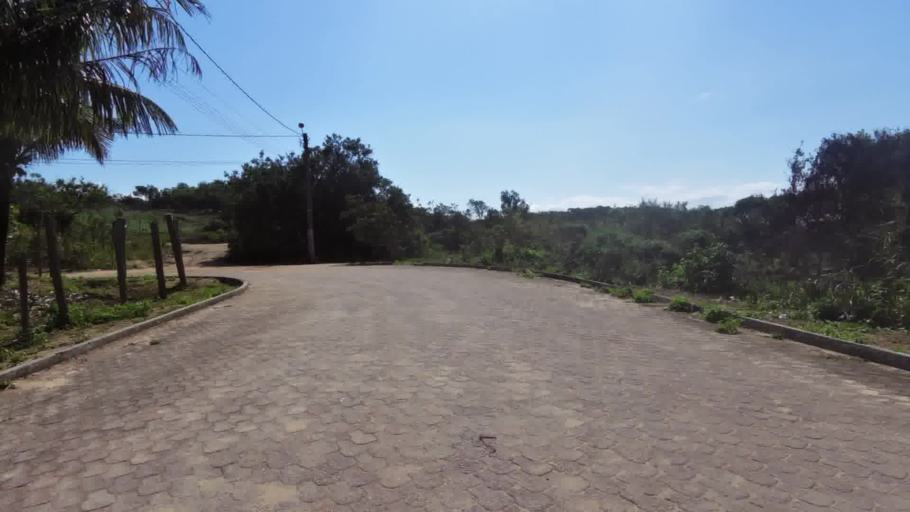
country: BR
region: Espirito Santo
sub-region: Piuma
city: Piuma
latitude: -20.8292
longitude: -40.6211
